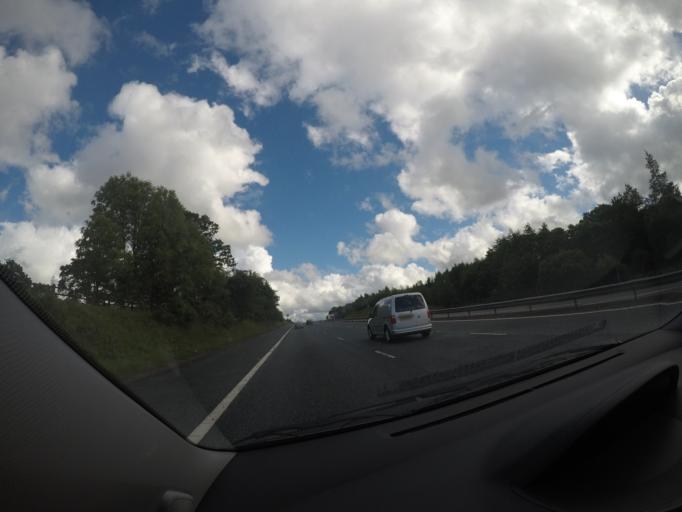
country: GB
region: Scotland
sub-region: South Lanarkshire
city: Douglas
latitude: 55.5679
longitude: -3.8074
